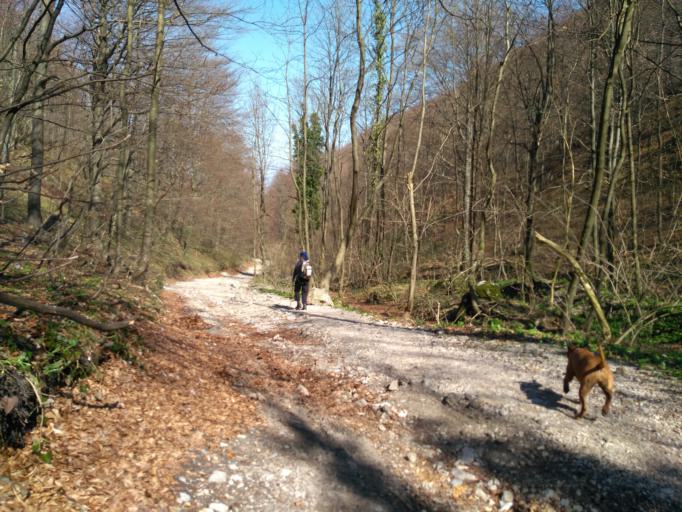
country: HR
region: Varazdinska
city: Ivanec
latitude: 46.1915
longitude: 16.1177
